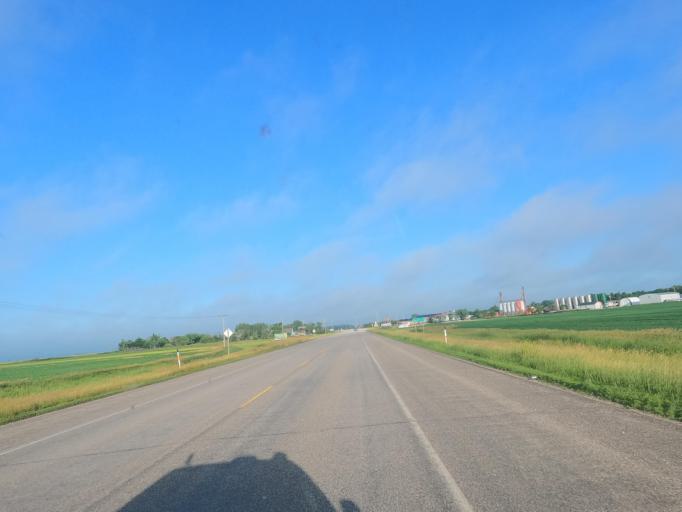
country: CA
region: Manitoba
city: Headingley
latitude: 49.7687
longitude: -97.6110
